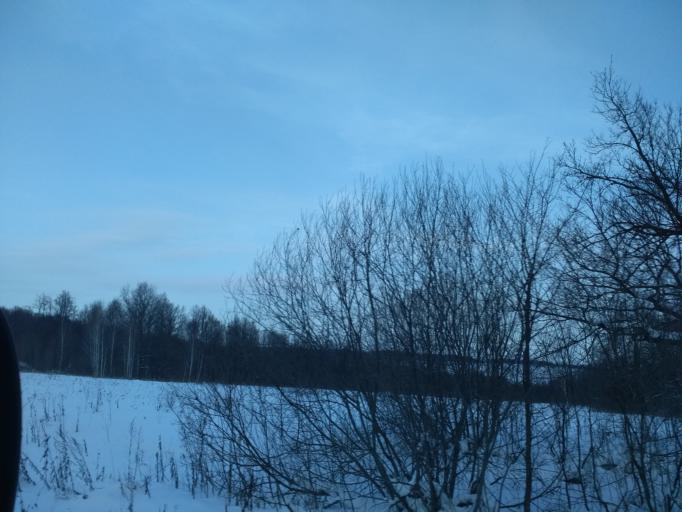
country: RU
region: Bashkortostan
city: Kudeyevskiy
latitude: 54.7202
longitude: 56.6077
